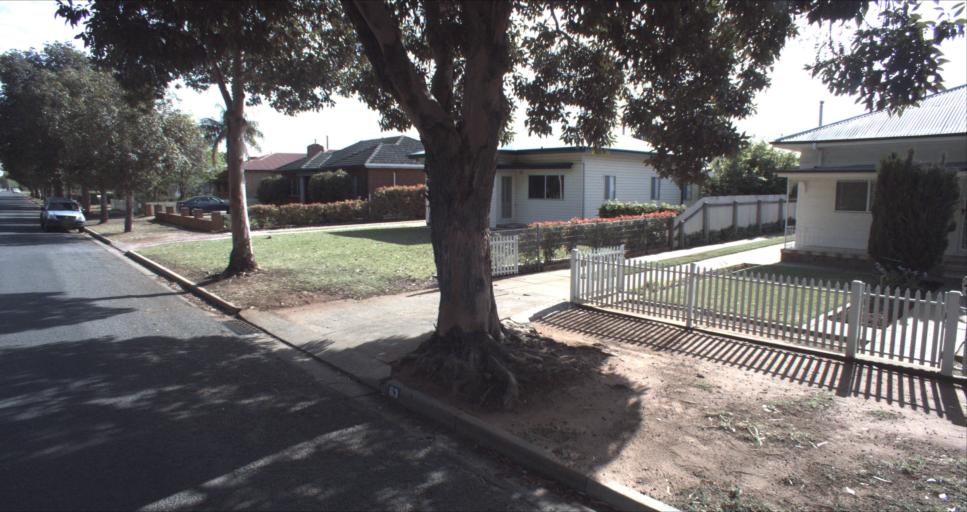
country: AU
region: New South Wales
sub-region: Leeton
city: Leeton
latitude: -34.5622
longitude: 146.4099
